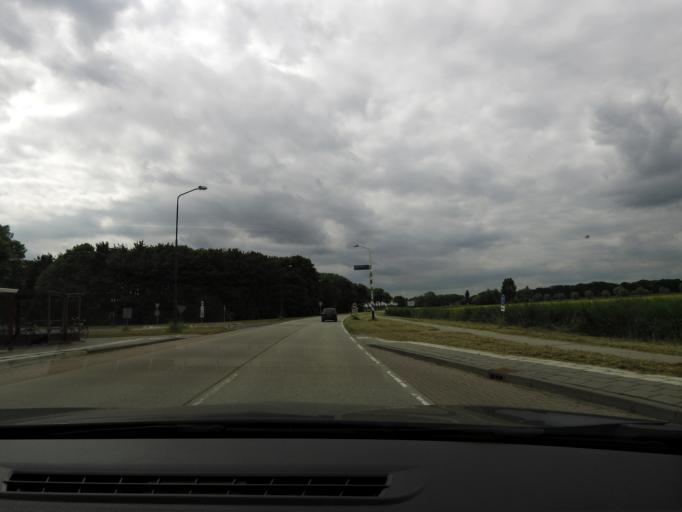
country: NL
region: North Brabant
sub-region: Gemeente Moerdijk
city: Klundert
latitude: 51.6543
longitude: 4.5426
